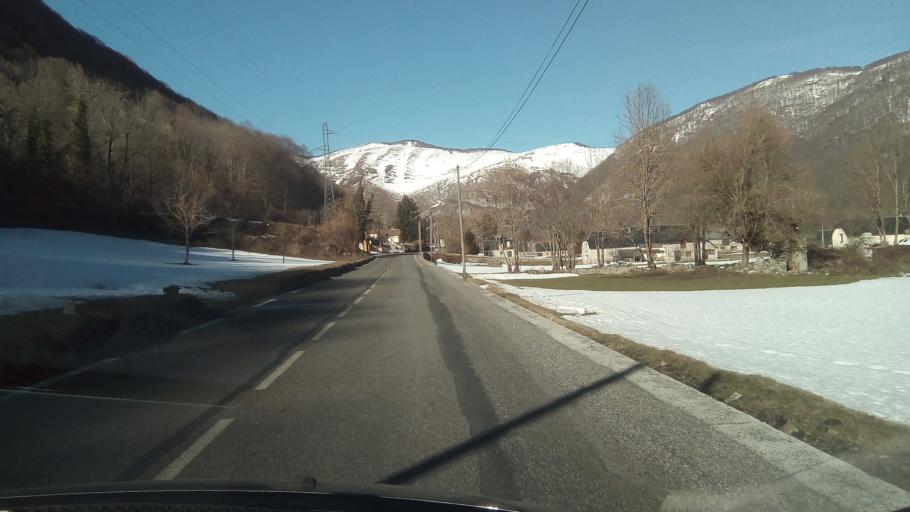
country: FR
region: Midi-Pyrenees
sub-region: Departement des Hautes-Pyrenees
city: Campan
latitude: 42.9629
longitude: 0.2315
